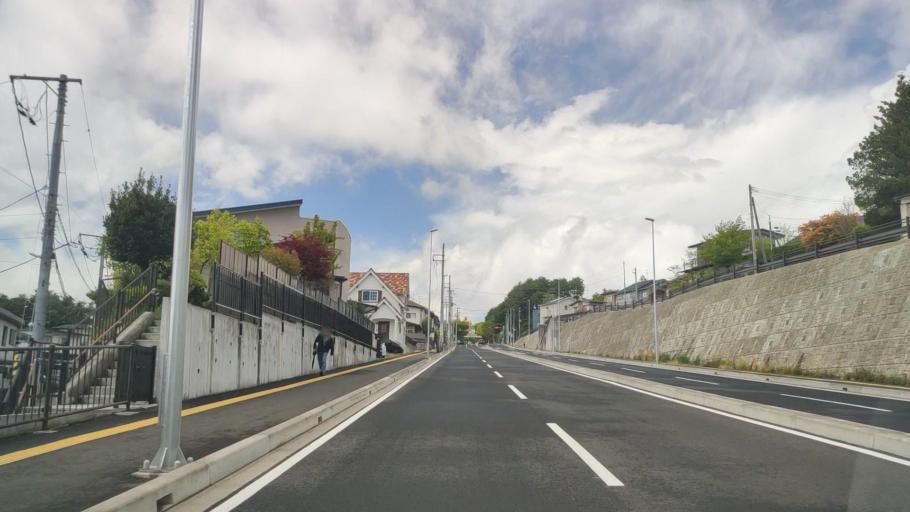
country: JP
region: Miyagi
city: Sendai
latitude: 38.2360
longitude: 140.8514
